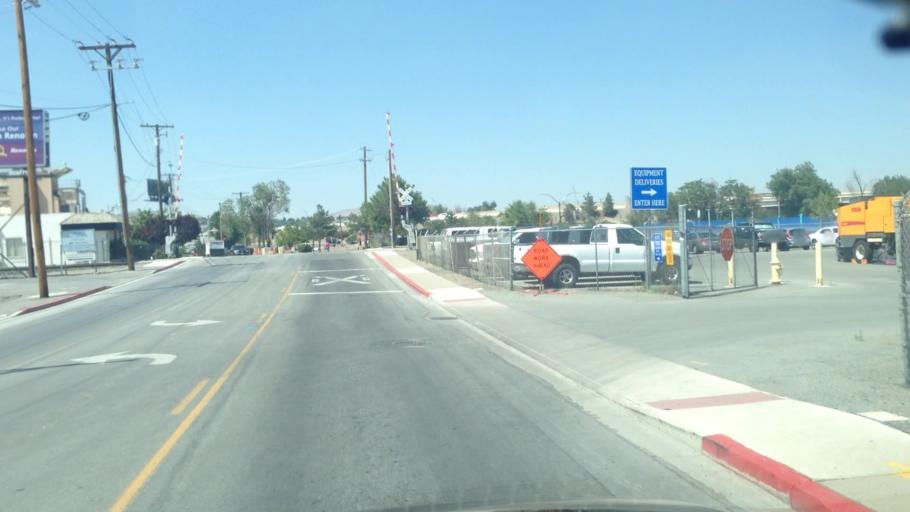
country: US
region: Nevada
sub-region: Washoe County
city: Sparks
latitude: 39.5334
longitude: -119.7804
